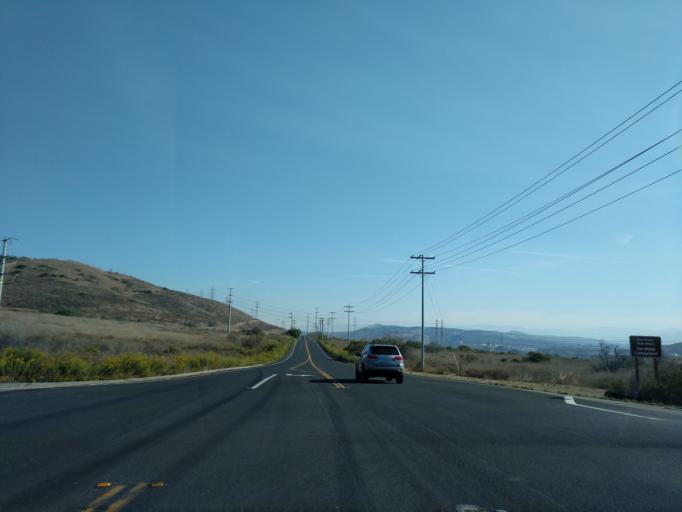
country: US
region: California
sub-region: Orange County
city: San Clemente
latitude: 33.4084
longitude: -117.5852
